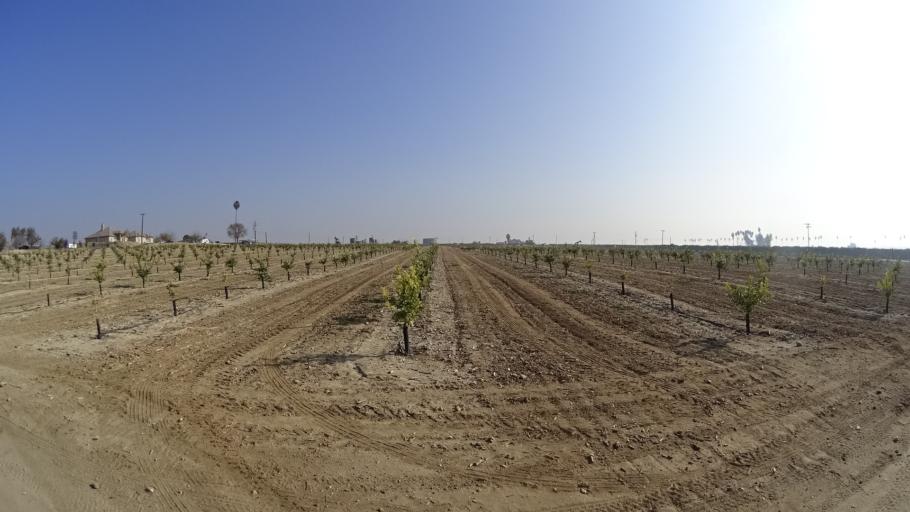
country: US
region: California
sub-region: Kern County
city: Lamont
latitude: 35.3628
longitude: -118.8788
